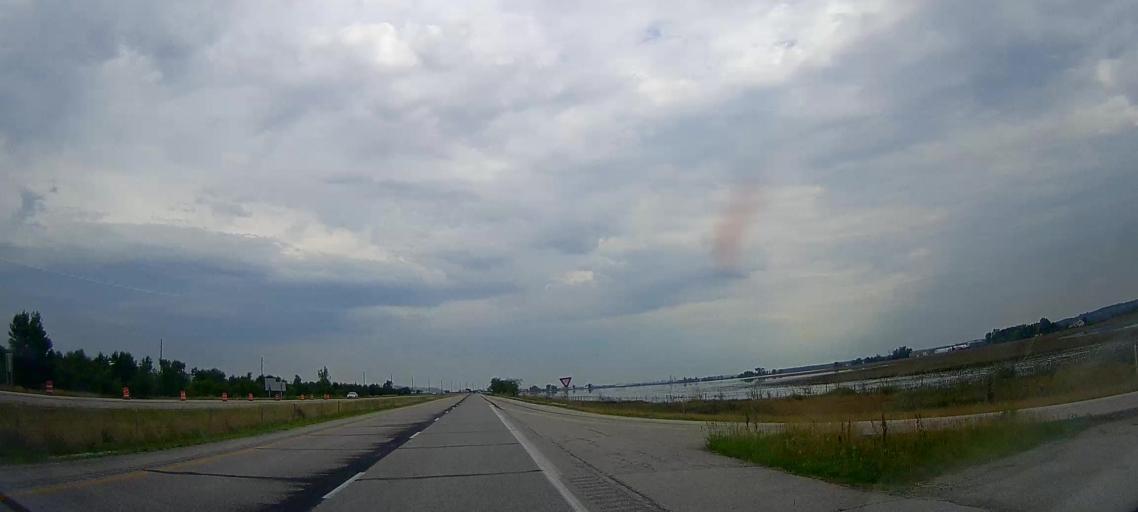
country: US
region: Iowa
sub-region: Pottawattamie County
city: Carter Lake
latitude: 41.4164
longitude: -95.9007
